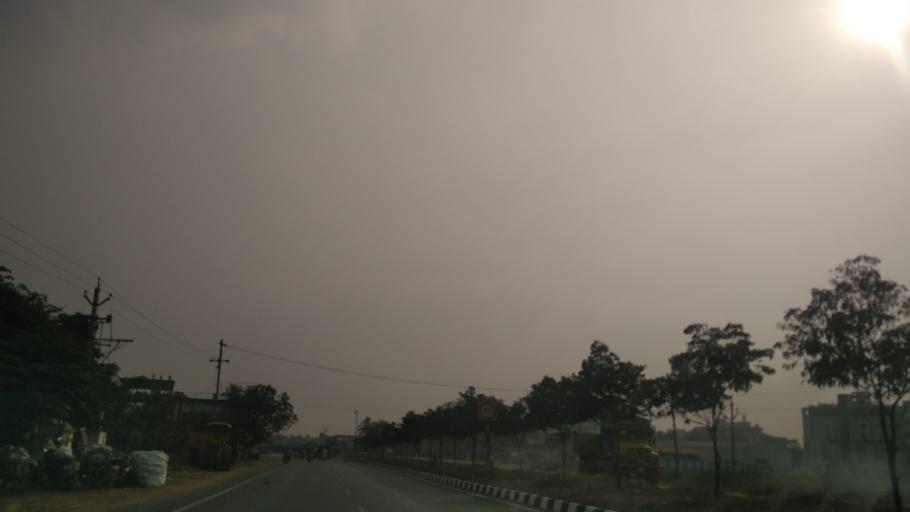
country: IN
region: Andhra Pradesh
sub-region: East Godavari
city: Rajahmundry
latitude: 16.9870
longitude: 81.7990
